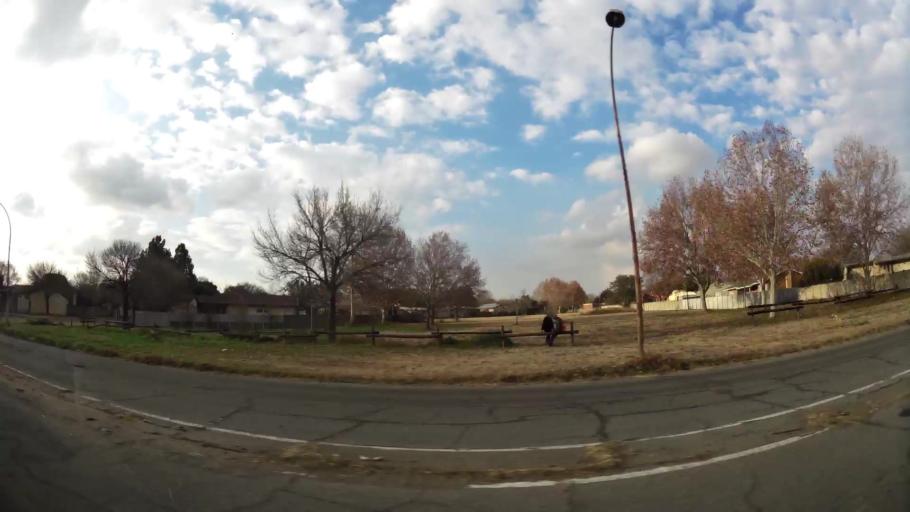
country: ZA
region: Orange Free State
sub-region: Fezile Dabi District Municipality
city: Sasolburg
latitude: -26.8223
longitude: 27.8100
